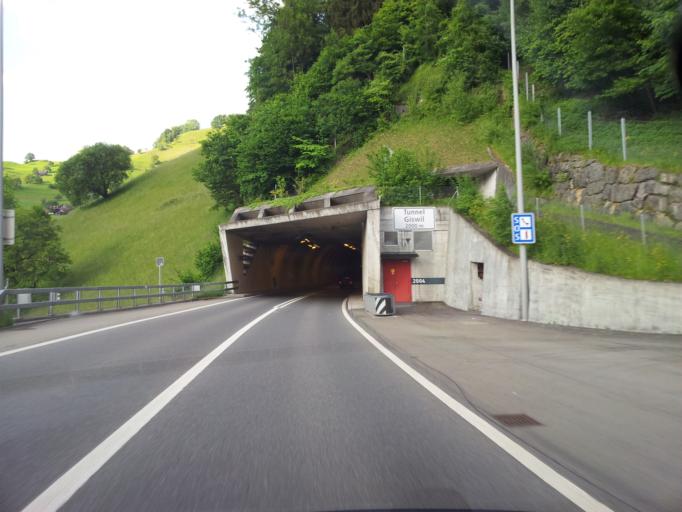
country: CH
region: Obwalden
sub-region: Obwalden
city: Giswil
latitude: 46.8257
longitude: 8.1837
